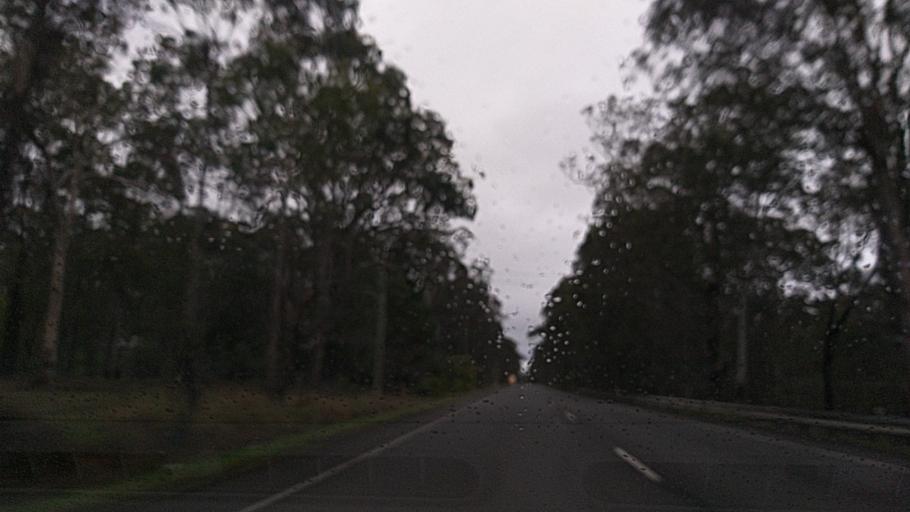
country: AU
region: New South Wales
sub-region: Wollondilly
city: Douglas Park
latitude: -34.2511
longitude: 150.7248
